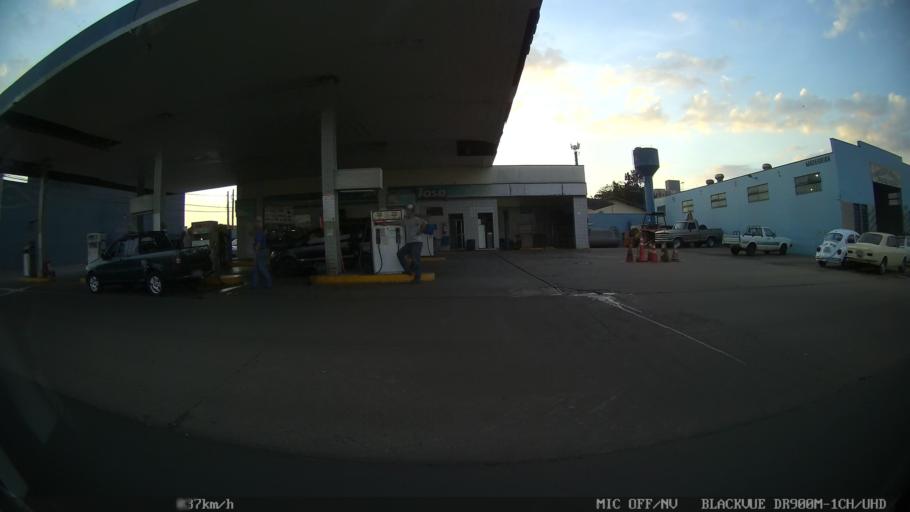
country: BR
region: Sao Paulo
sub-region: Ribeirao Preto
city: Ribeirao Preto
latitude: -21.1356
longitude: -47.8181
